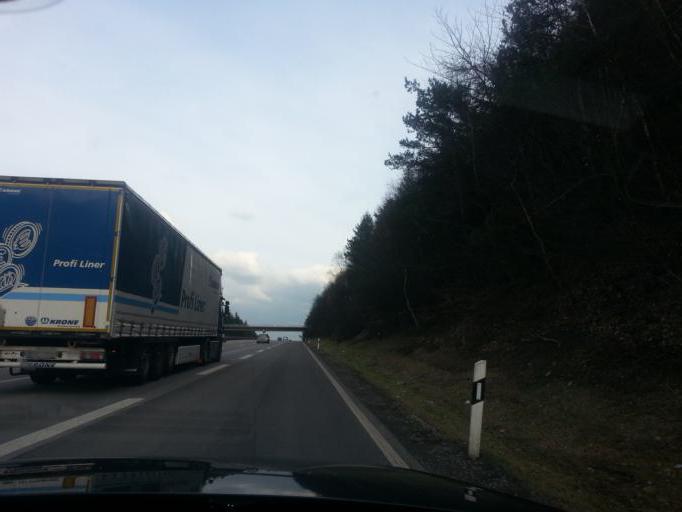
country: DE
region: Rheinland-Pfalz
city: Mehlingen
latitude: 49.4569
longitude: 7.8465
